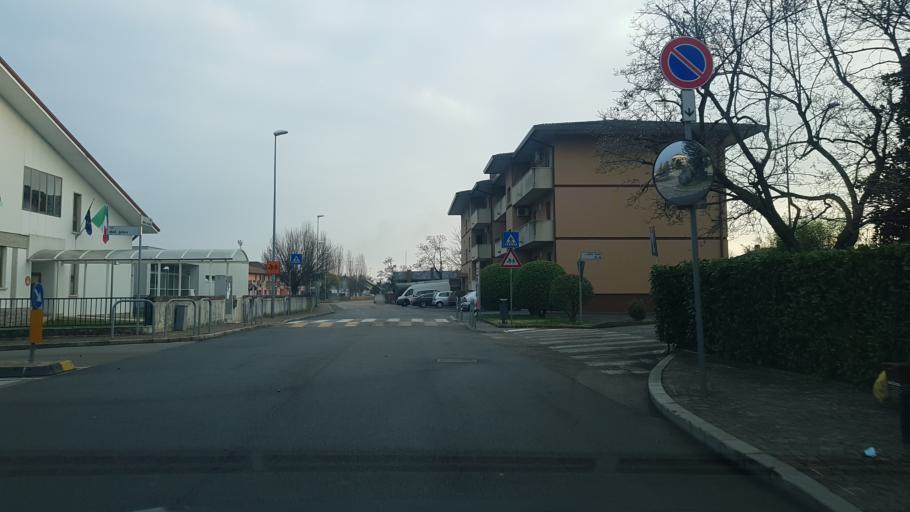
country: IT
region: Friuli Venezia Giulia
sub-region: Provincia di Udine
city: San Giovanni al Natisone
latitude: 45.9764
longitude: 13.4006
